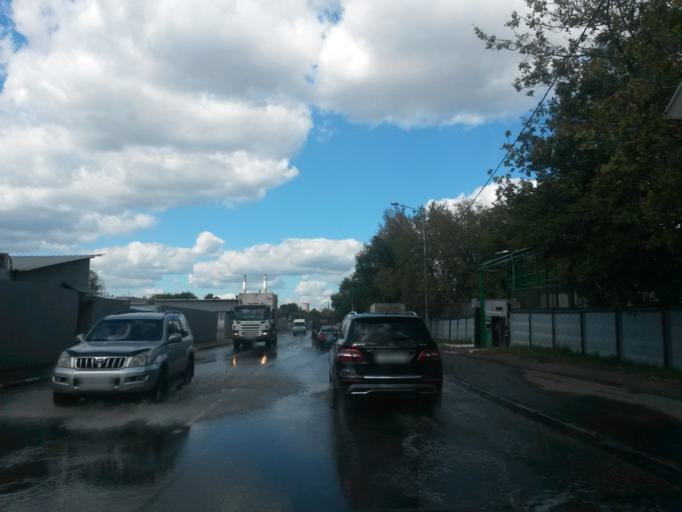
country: RU
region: Moskovskaya
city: Kozhukhovo
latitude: 55.7046
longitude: 37.7026
